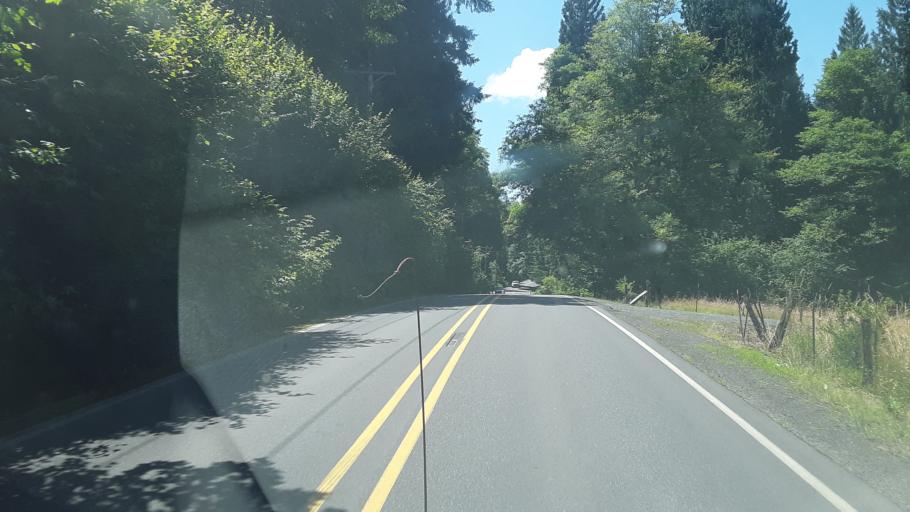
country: US
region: Washington
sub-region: Clark County
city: Amboy
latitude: 45.8957
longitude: -122.4686
